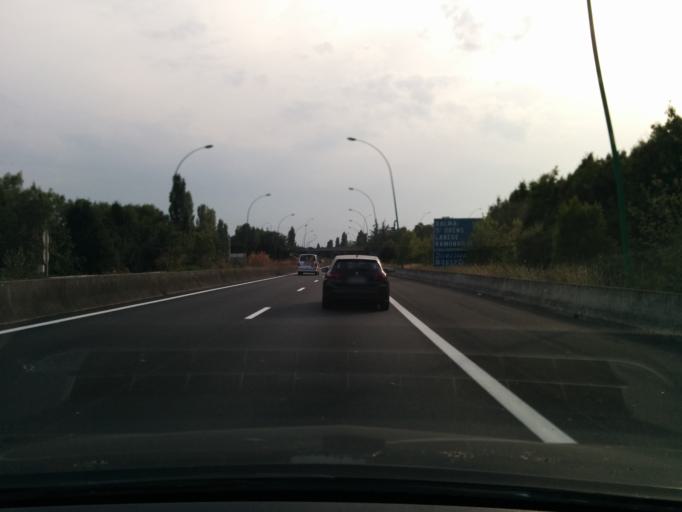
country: FR
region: Midi-Pyrenees
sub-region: Departement de la Haute-Garonne
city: Saint-Jean
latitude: 43.6442
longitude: 1.4974
